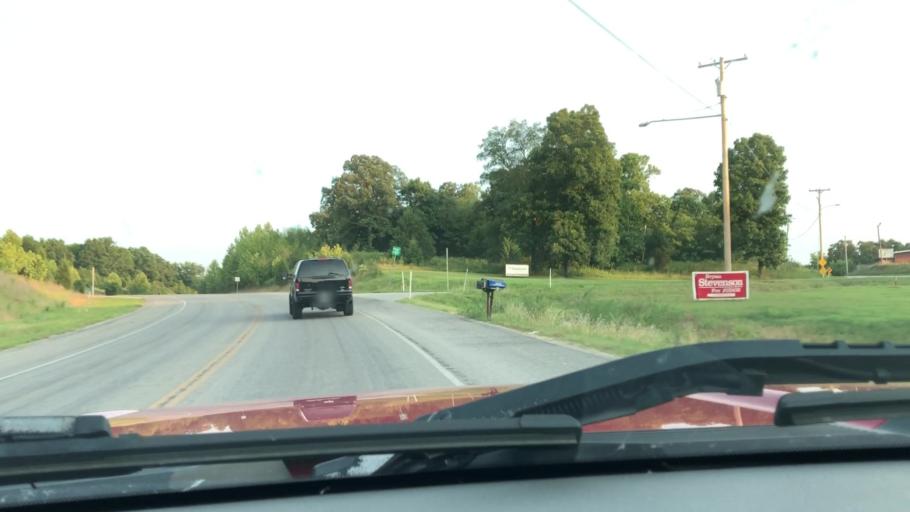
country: US
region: Missouri
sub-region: Jasper County
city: Joplin
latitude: 37.0256
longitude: -94.5151
